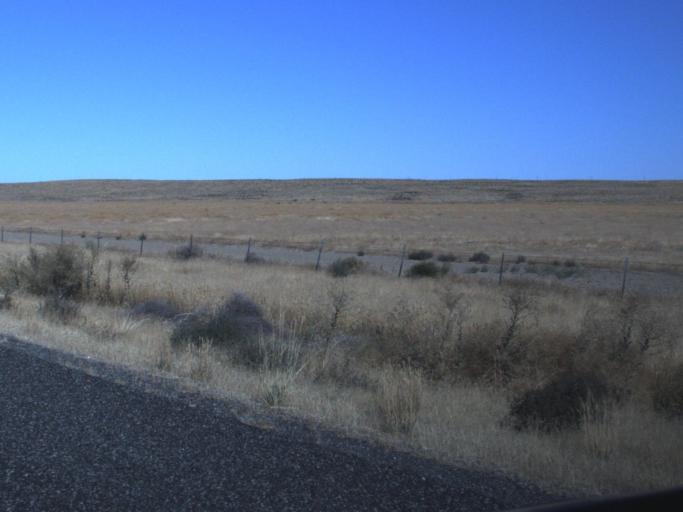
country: US
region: Washington
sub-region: Benton County
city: Benton City
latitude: 46.4833
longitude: -119.5760
